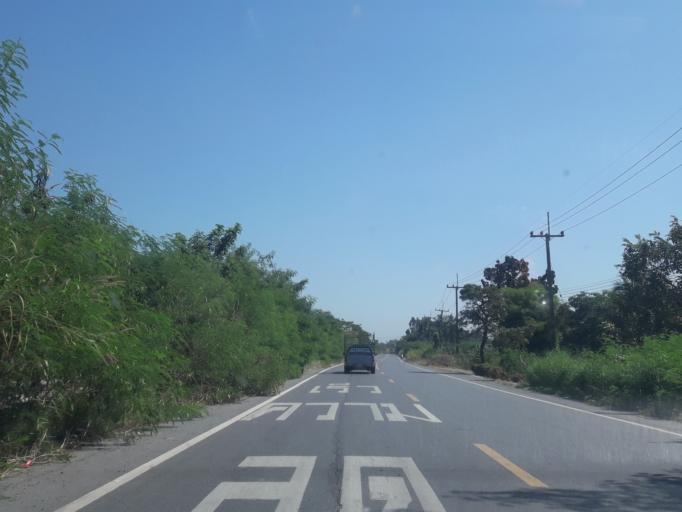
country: TH
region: Sara Buri
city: Nong Khae
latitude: 14.3155
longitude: 100.8579
